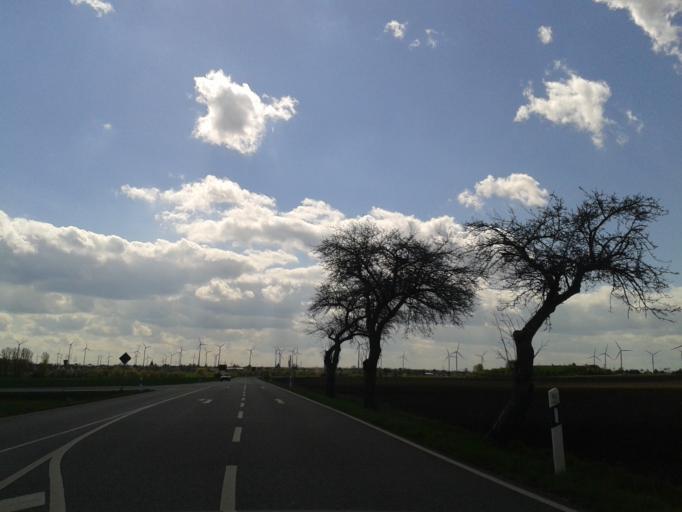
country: DE
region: Saxony-Anhalt
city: Wansleben
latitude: 51.4223
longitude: 11.7564
